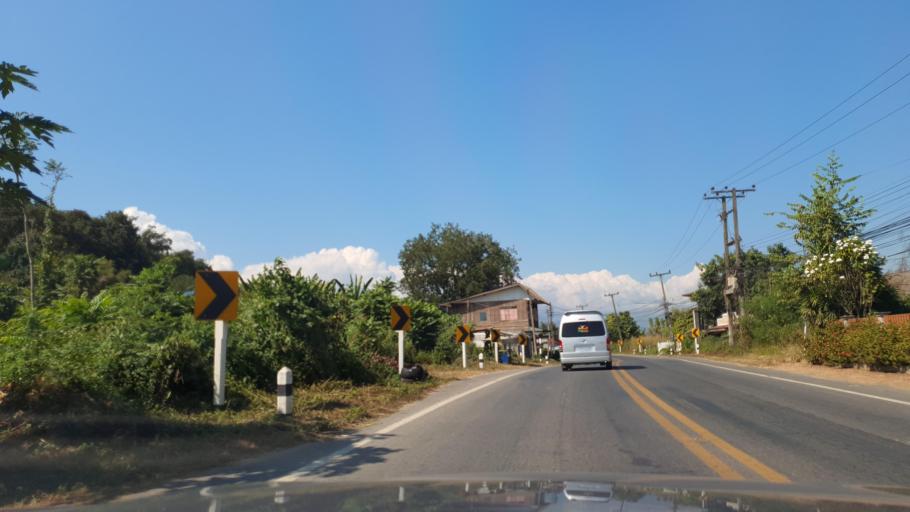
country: TH
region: Nan
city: Tha Wang Pha
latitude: 19.1055
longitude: 100.8141
